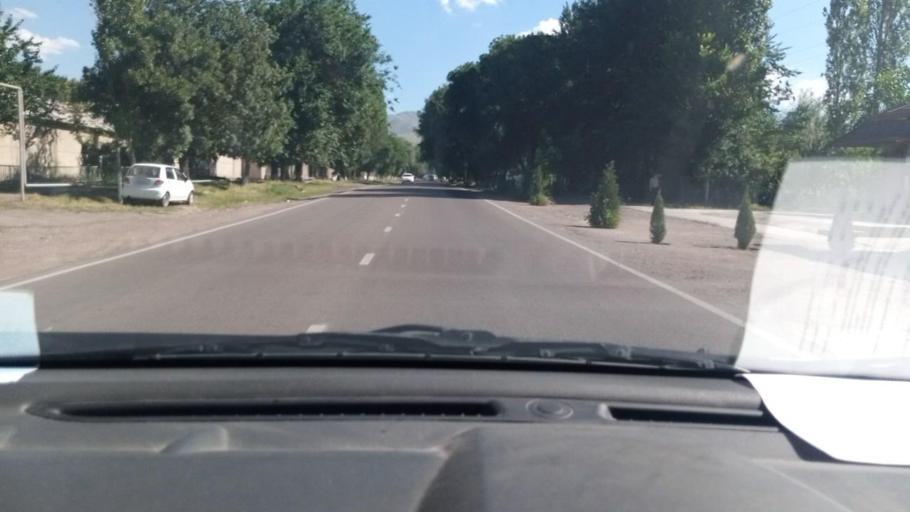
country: UZ
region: Toshkent
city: Angren
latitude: 41.0332
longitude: 70.0920
